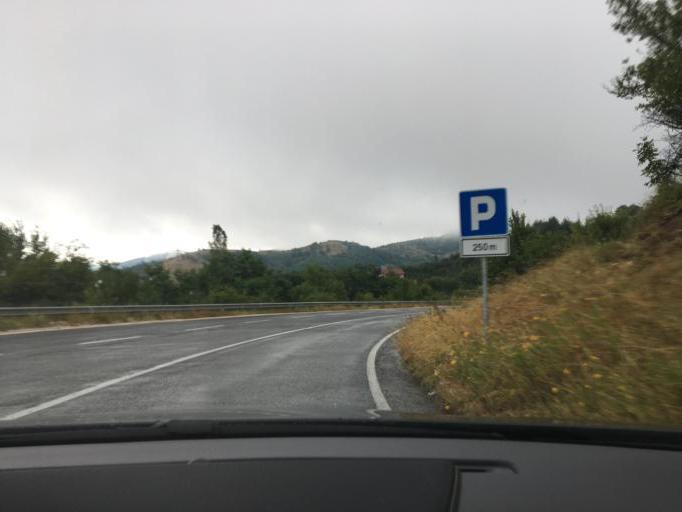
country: MK
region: Kriva Palanka
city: Kriva Palanka
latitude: 42.2167
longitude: 22.4502
